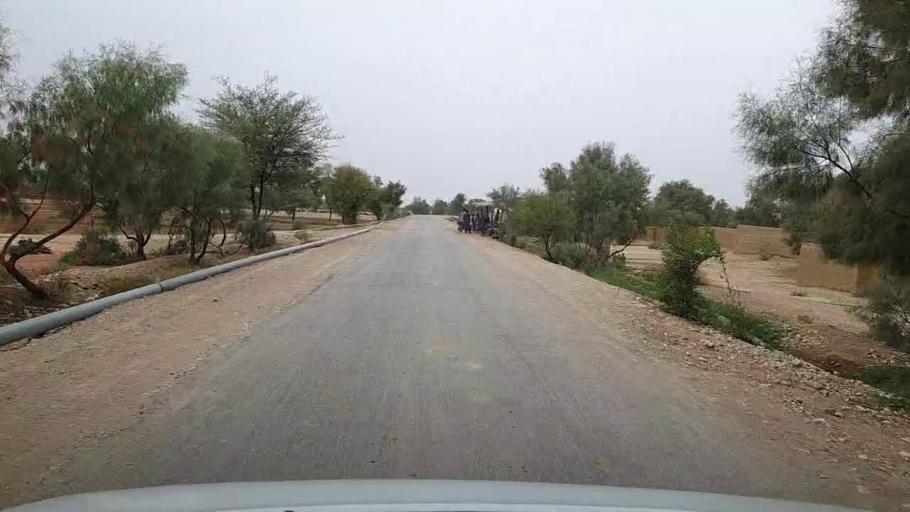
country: PK
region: Sindh
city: Sehwan
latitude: 26.3219
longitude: 67.7299
